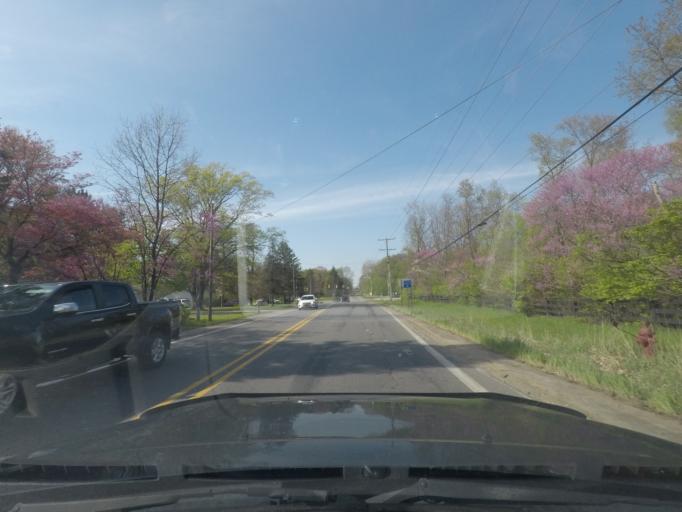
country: US
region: Michigan
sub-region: Berrien County
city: Niles
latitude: 41.7999
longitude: -86.2545
